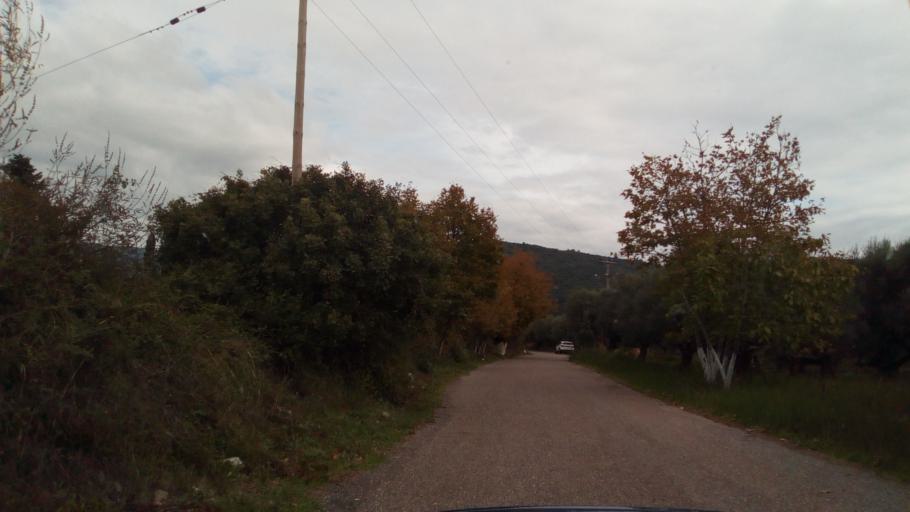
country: GR
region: West Greece
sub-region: Nomos Achaias
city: Kamarai
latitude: 38.4187
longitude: 21.9548
